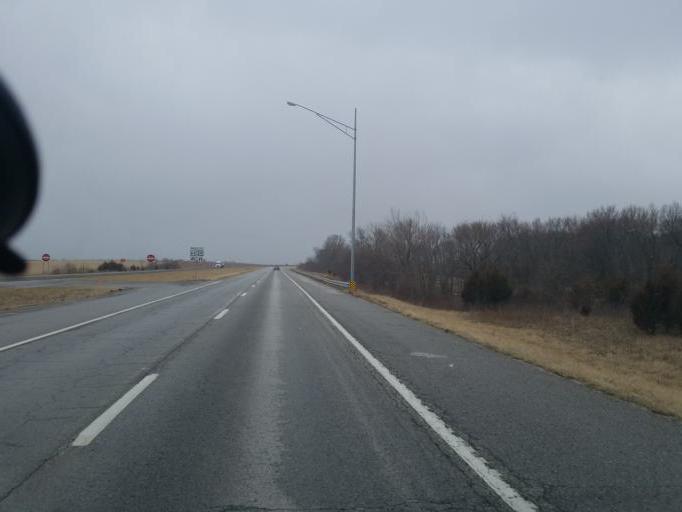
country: US
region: Missouri
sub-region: Macon County
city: La Plata
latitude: 39.8928
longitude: -92.4714
